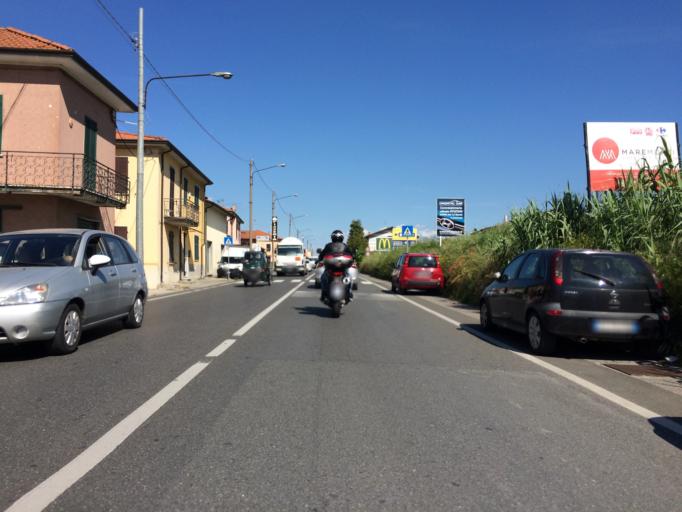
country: IT
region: Liguria
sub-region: Provincia di La Spezia
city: Casano-Dogana-Isola
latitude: 44.0690
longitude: 10.0264
